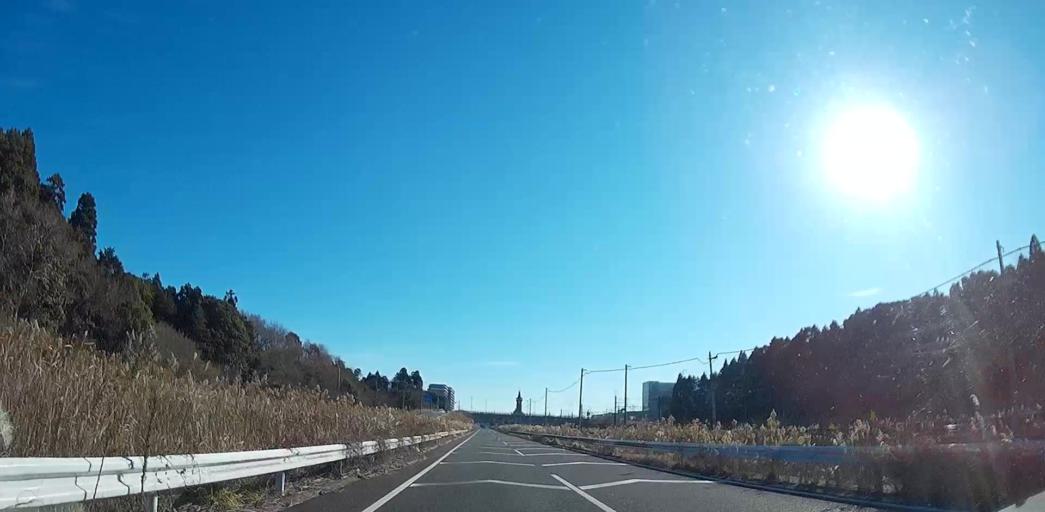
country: JP
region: Chiba
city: Sakura
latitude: 35.7899
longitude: 140.1974
